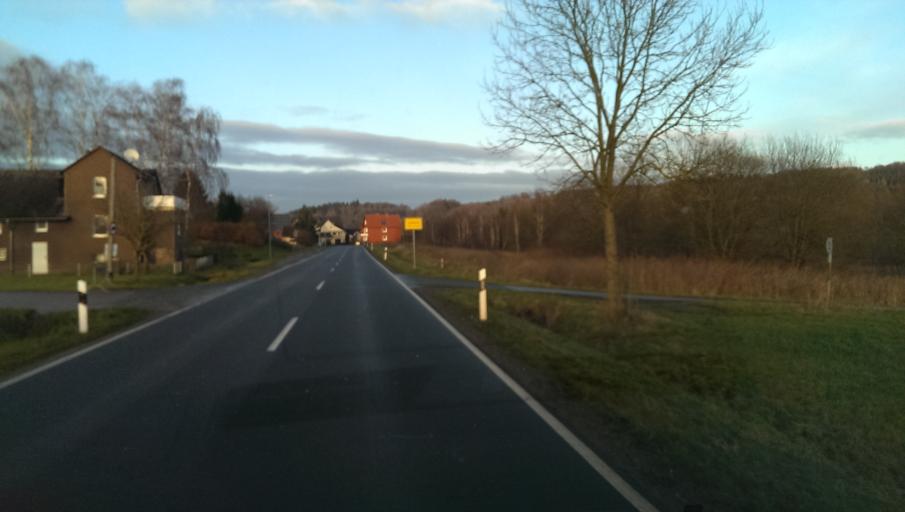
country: DE
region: Lower Saxony
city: Lenne
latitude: 51.8871
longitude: 9.6819
